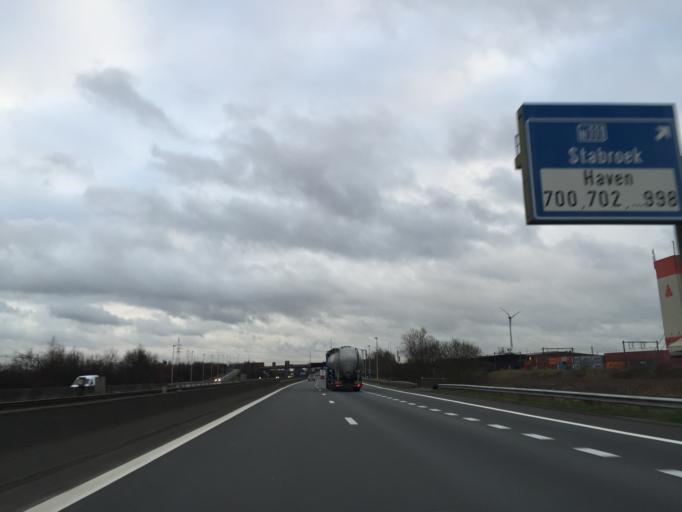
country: BE
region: Flanders
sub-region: Provincie Antwerpen
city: Stabroek
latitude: 51.3297
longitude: 4.3489
